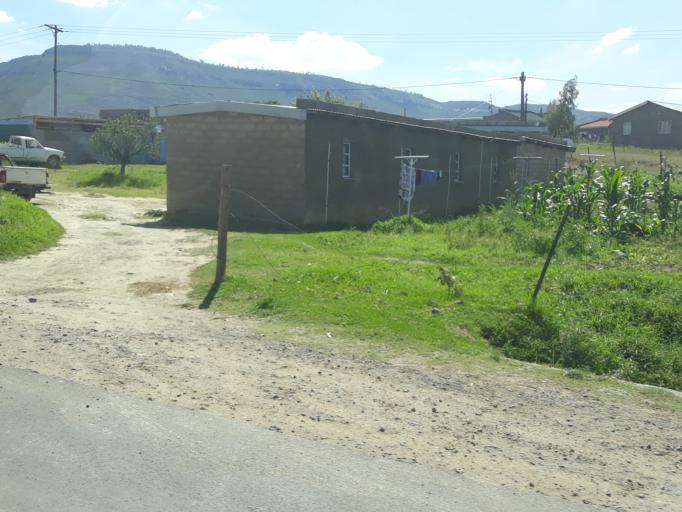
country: LS
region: Mohale's Hoek District
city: Mohale's Hoek
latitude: -30.1094
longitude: 27.4689
